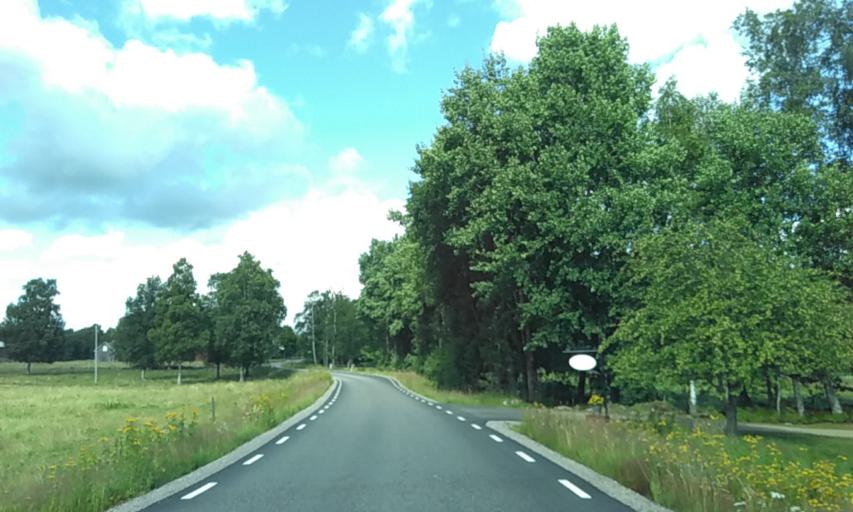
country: SE
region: Vaestra Goetaland
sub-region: Vargarda Kommun
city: Vargarda
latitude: 57.9694
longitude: 12.8982
